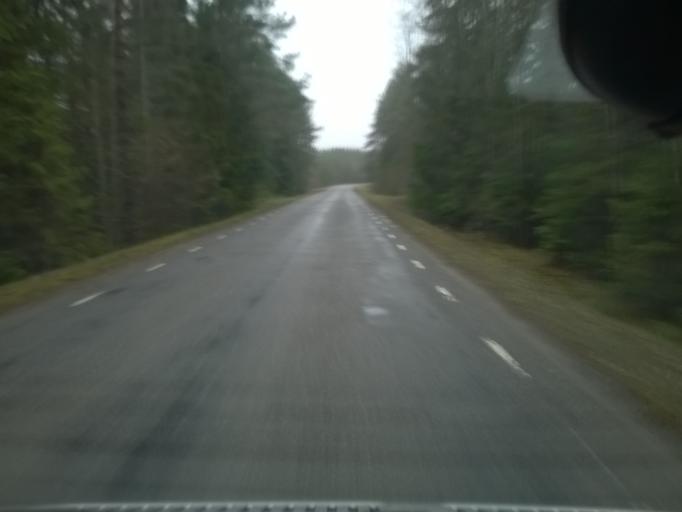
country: EE
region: Raplamaa
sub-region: Kohila vald
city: Kohila
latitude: 59.1921
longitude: 24.6625
